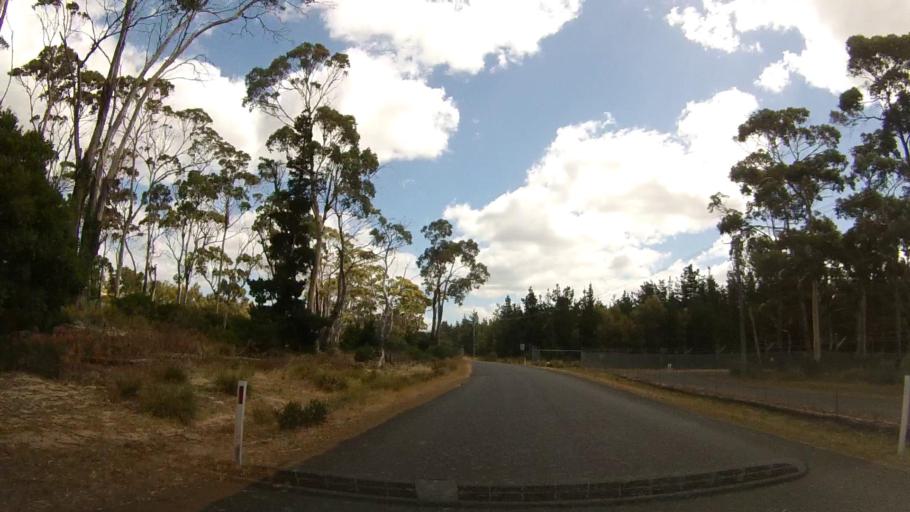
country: AU
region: Tasmania
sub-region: Clarence
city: Seven Mile Beach
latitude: -42.8485
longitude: 147.5223
